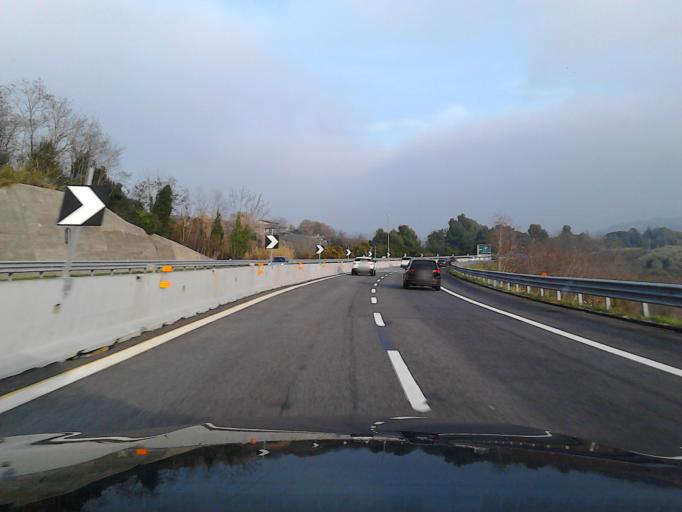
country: IT
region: Abruzzo
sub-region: Provincia di Chieti
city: Francavilla al Mare
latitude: 42.4179
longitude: 14.2459
